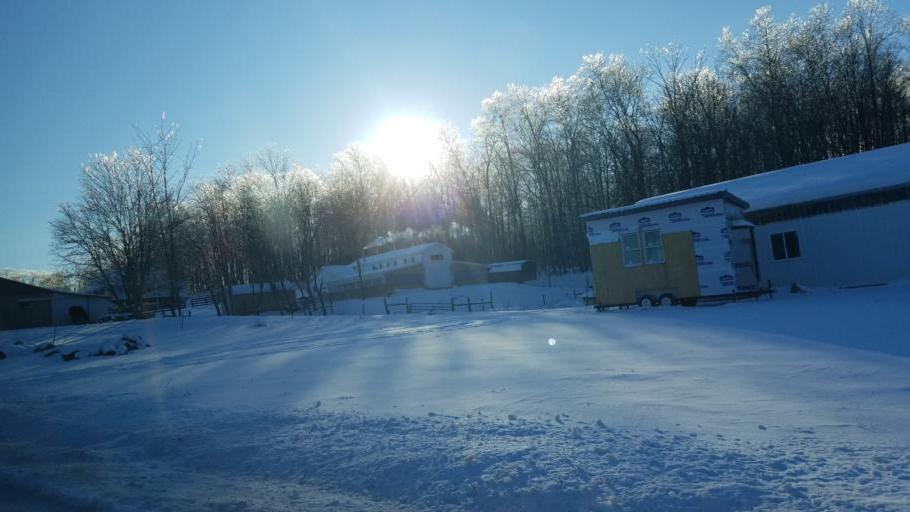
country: US
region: Ohio
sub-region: Knox County
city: Fredericktown
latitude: 40.4991
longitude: -82.6059
